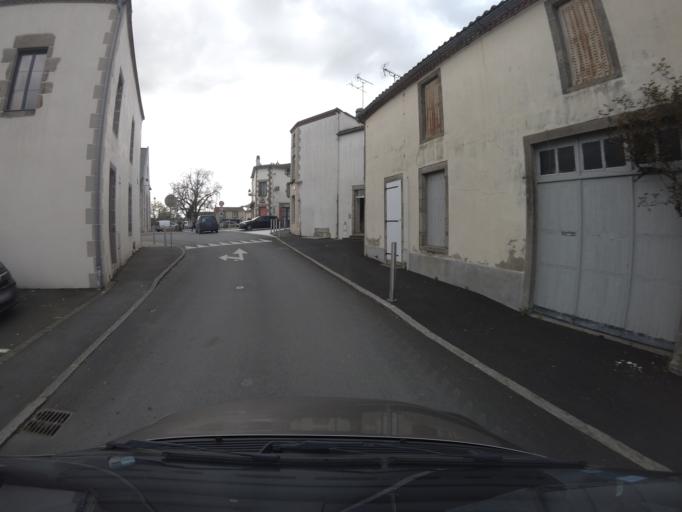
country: FR
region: Pays de la Loire
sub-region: Departement de la Vendee
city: Montaigu
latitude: 46.9756
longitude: -1.3124
